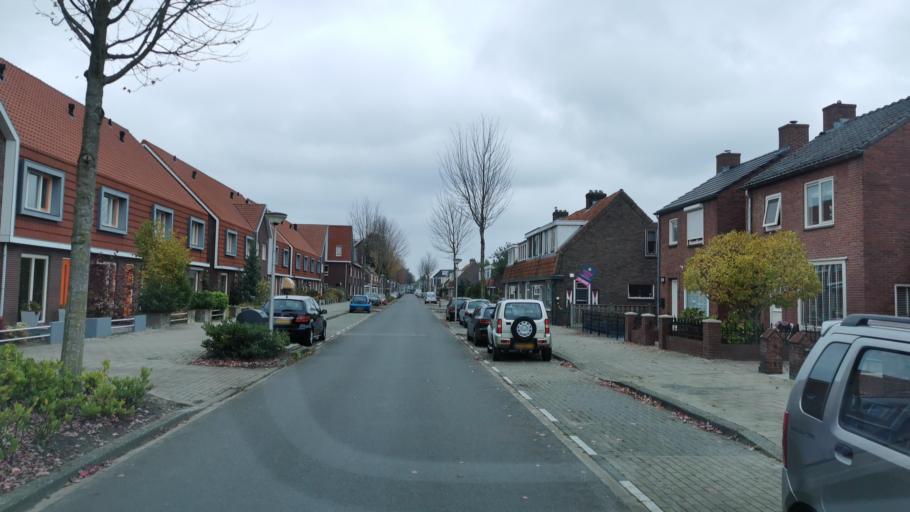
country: DE
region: North Rhine-Westphalia
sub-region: Regierungsbezirk Munster
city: Gronau
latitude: 52.2136
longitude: 6.9640
